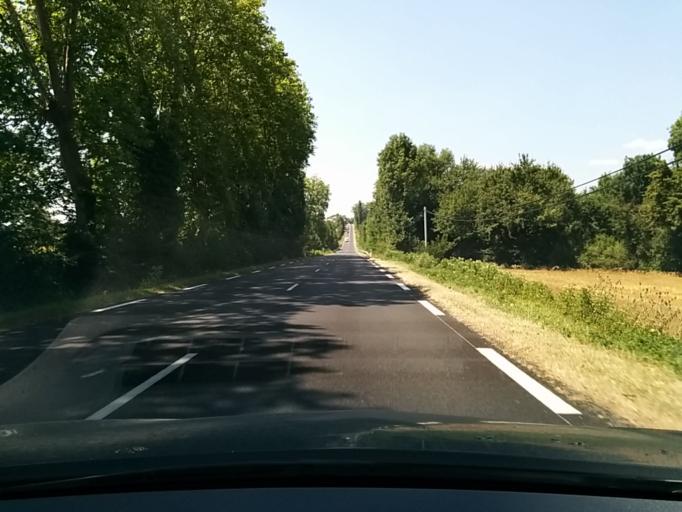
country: FR
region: Midi-Pyrenees
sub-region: Departement du Gers
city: Gimont
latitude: 43.6237
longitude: 0.8976
